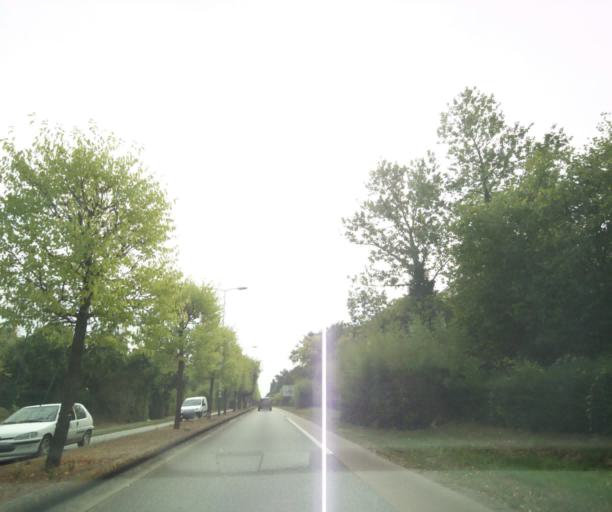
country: FR
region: Pays de la Loire
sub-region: Departement de la Loire-Atlantique
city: Saint-Herblain
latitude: 47.2165
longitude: -1.6420
